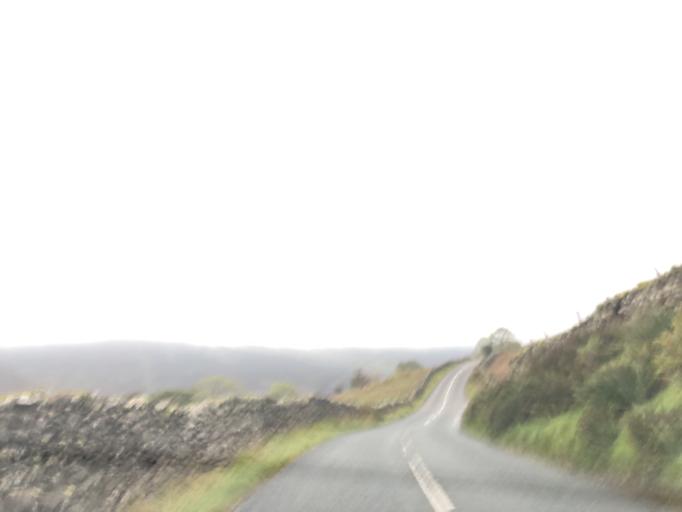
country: GB
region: England
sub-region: Cumbria
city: Ambleside
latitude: 54.4481
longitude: -2.9064
